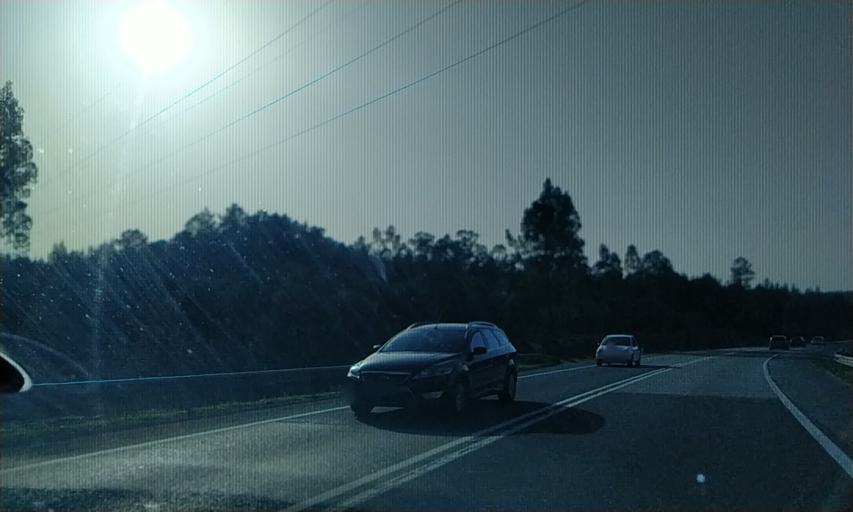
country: PT
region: Leiria
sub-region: Leiria
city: Leiria
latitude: 39.7432
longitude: -8.8423
